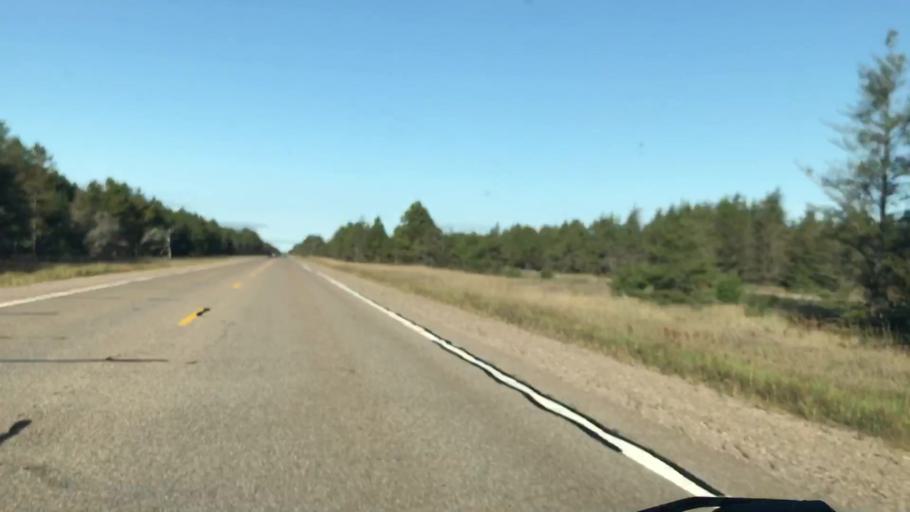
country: US
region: Michigan
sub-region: Chippewa County
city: Sault Ste. Marie
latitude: 46.3587
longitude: -84.8239
